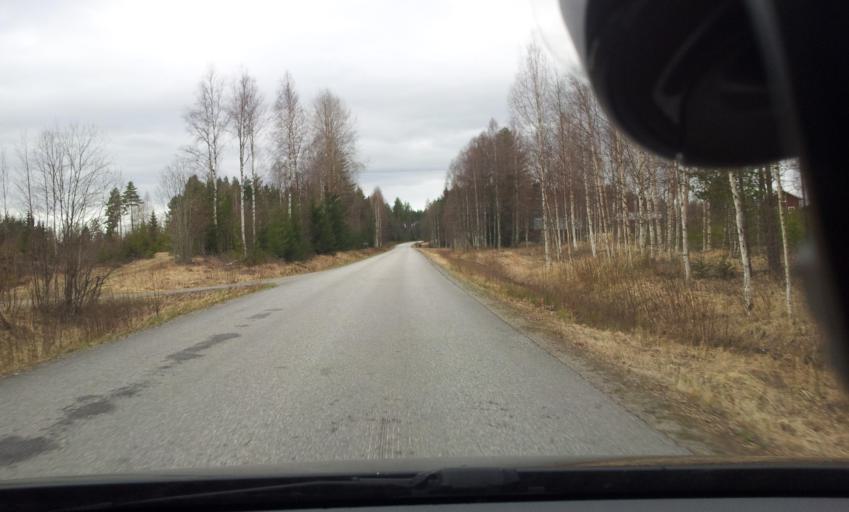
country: SE
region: Gaevleborg
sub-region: Ljusdals Kommun
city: Ljusdal
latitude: 61.8259
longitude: 15.9920
